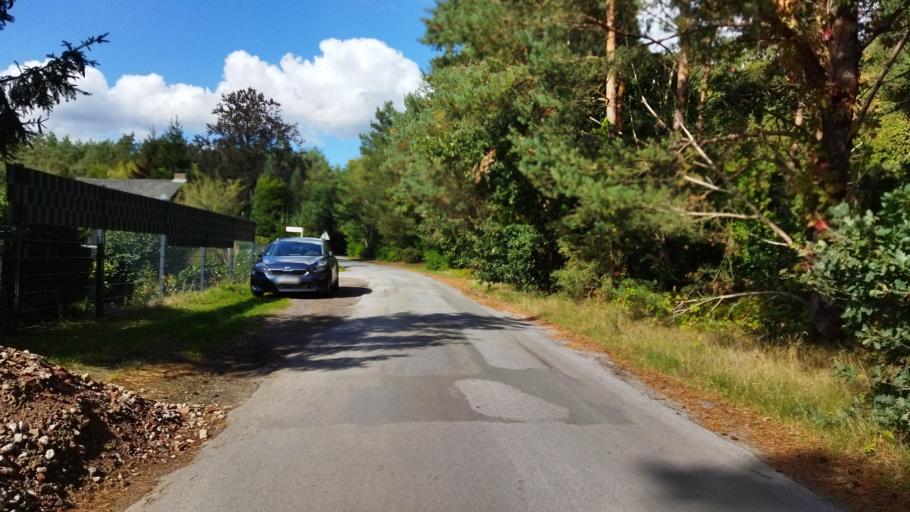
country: DE
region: Lower Saxony
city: Emsburen
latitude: 52.4282
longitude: 7.3414
